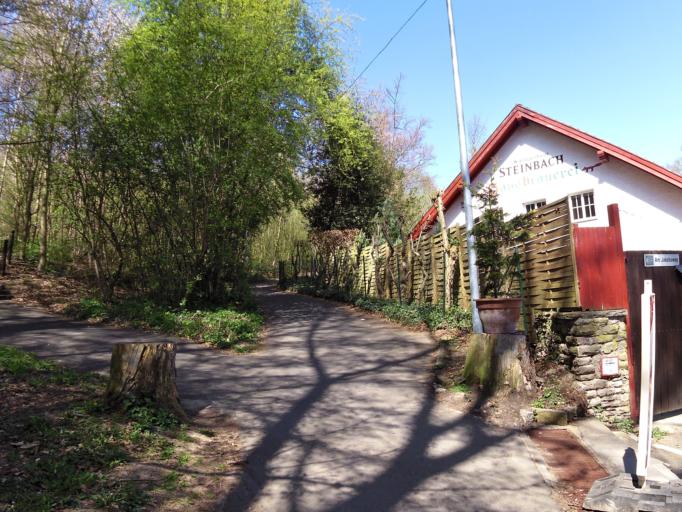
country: DE
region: North Rhine-Westphalia
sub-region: Regierungsbezirk Koln
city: Bad Munstereifel
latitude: 50.5884
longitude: 6.8310
